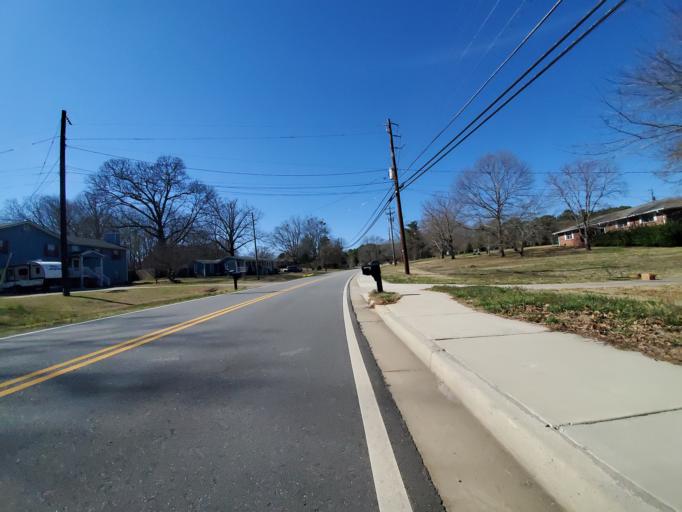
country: US
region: Georgia
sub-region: Gwinnett County
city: Dacula
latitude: 33.9817
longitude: -83.8820
